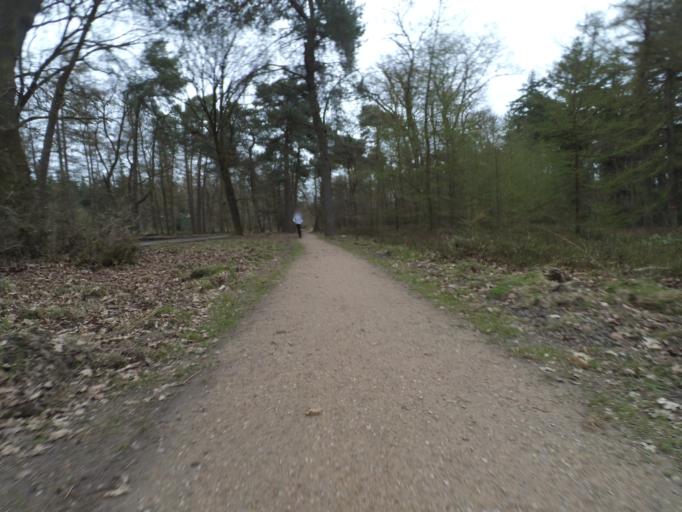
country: NL
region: Gelderland
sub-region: Gemeente Apeldoorn
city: Loenen
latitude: 52.0963
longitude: 5.9929
